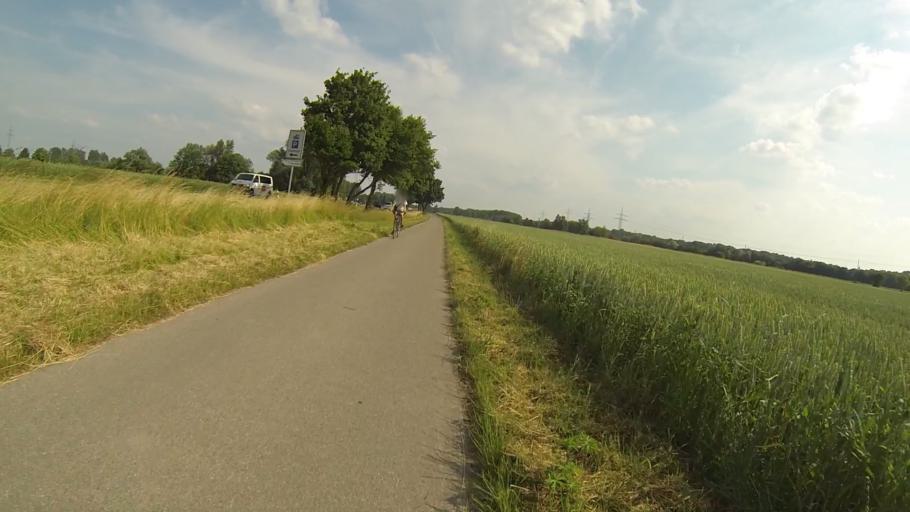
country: DE
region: Bavaria
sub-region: Swabia
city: Neu-Ulm
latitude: 48.3615
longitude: 10.0119
